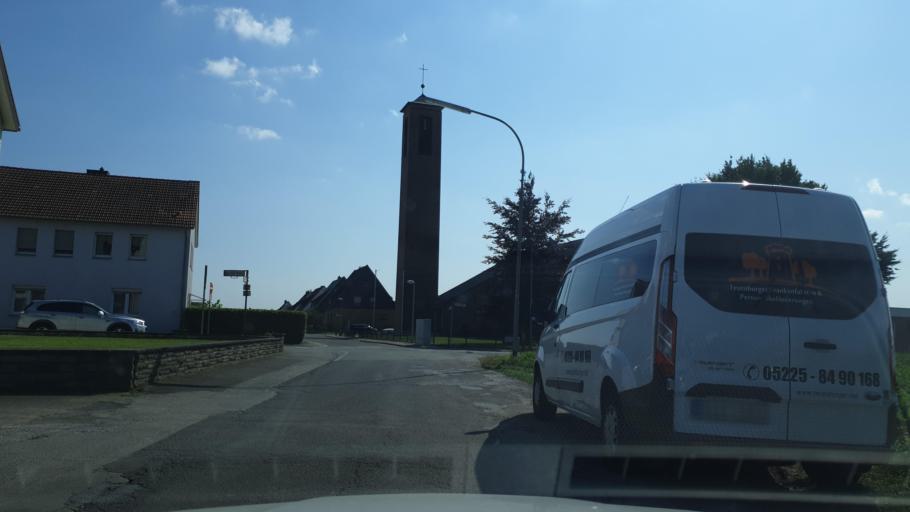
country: DE
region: North Rhine-Westphalia
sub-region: Regierungsbezirk Detmold
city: Hiddenhausen
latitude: 52.1289
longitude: 8.6222
